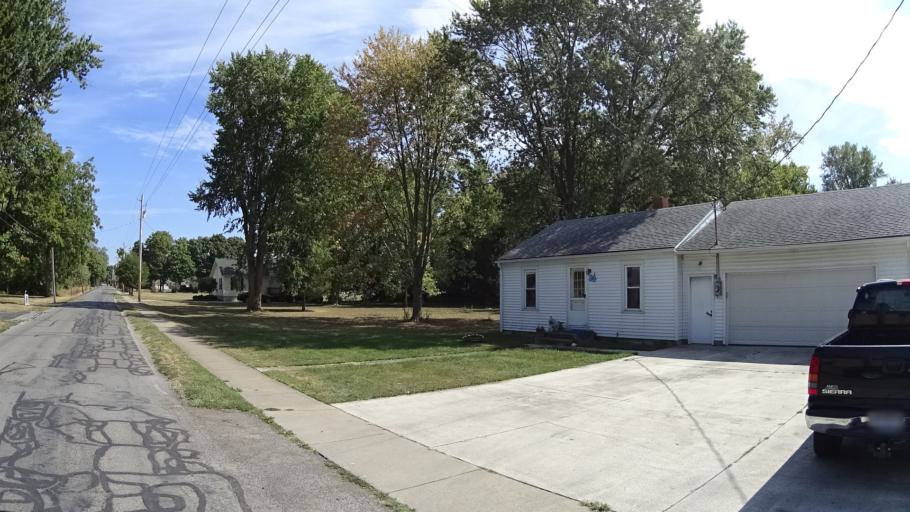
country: US
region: Ohio
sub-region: Erie County
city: Sandusky
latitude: 41.5968
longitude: -82.7094
